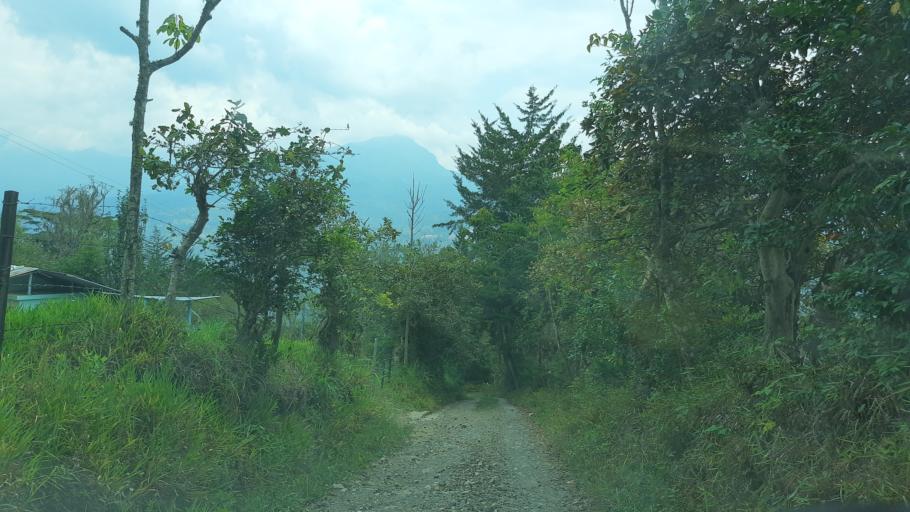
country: CO
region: Cundinamarca
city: Tenza
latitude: 5.0814
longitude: -73.3969
